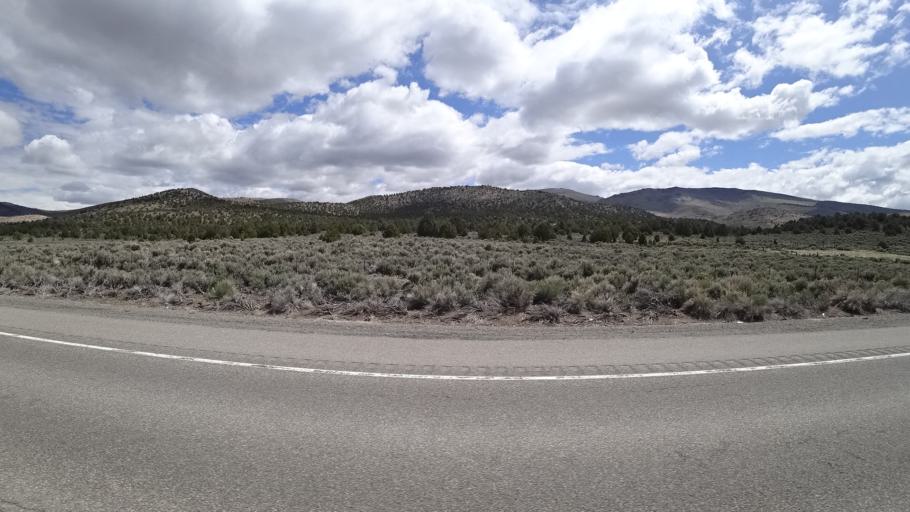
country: US
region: Nevada
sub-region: Douglas County
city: Gardnerville Ranchos
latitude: 38.7953
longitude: -119.6011
